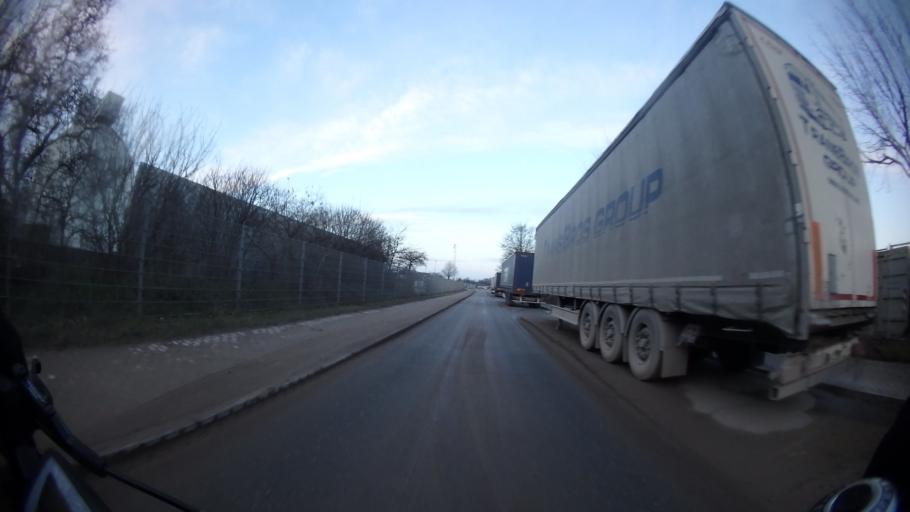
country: DE
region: Mecklenburg-Vorpommern
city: Selmsdorf
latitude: 53.8992
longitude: 10.8117
